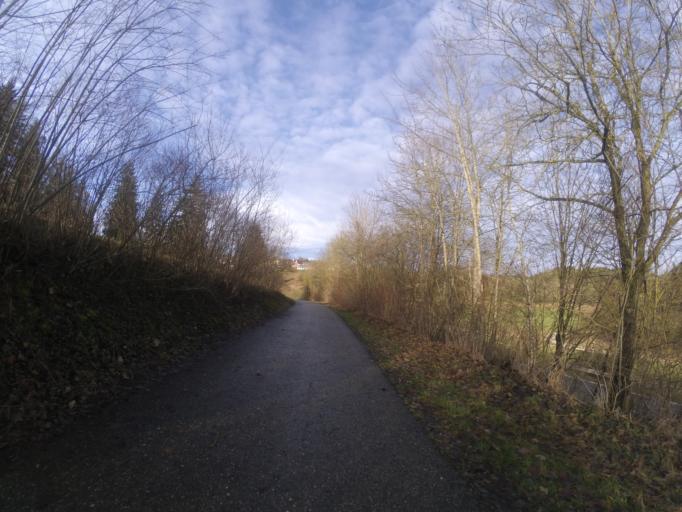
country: DE
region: Baden-Wuerttemberg
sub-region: Tuebingen Region
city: Dornstadt
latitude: 48.4350
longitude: 9.9487
